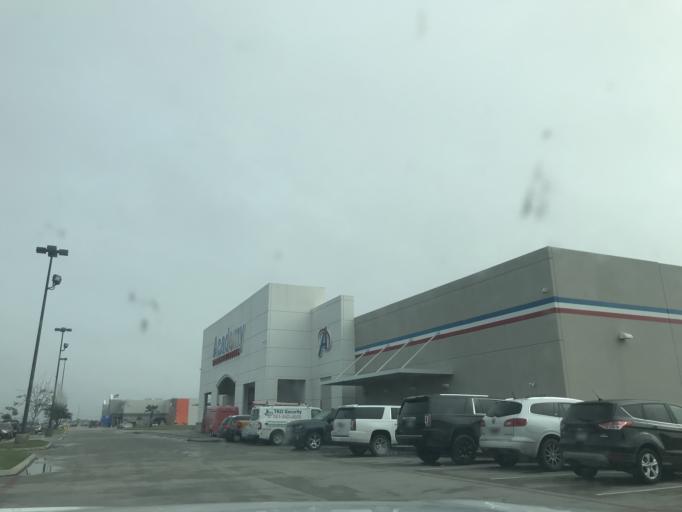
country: US
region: Texas
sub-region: San Patricio County
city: Portland
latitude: 27.8927
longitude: -97.3074
